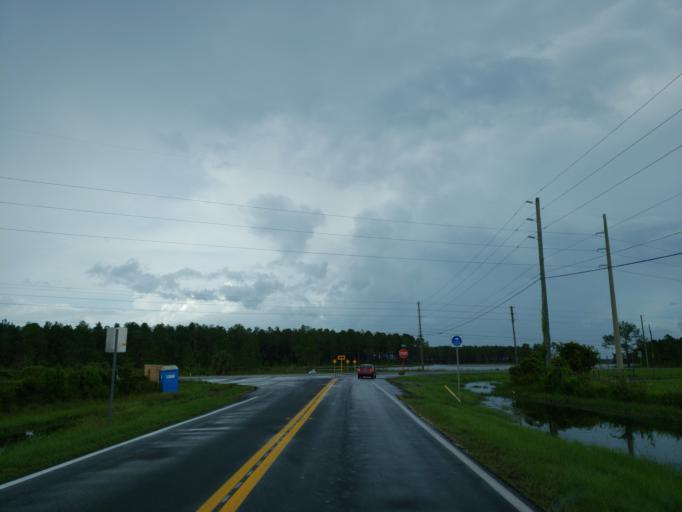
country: US
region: Florida
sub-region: Pasco County
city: Land O' Lakes
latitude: 28.3226
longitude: -82.4168
